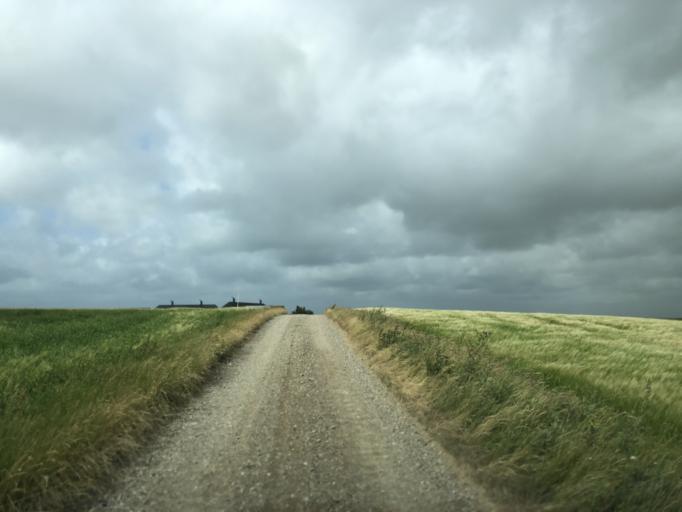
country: DK
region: Central Jutland
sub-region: Lemvig Kommune
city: Harboore
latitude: 56.5117
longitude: 8.1283
